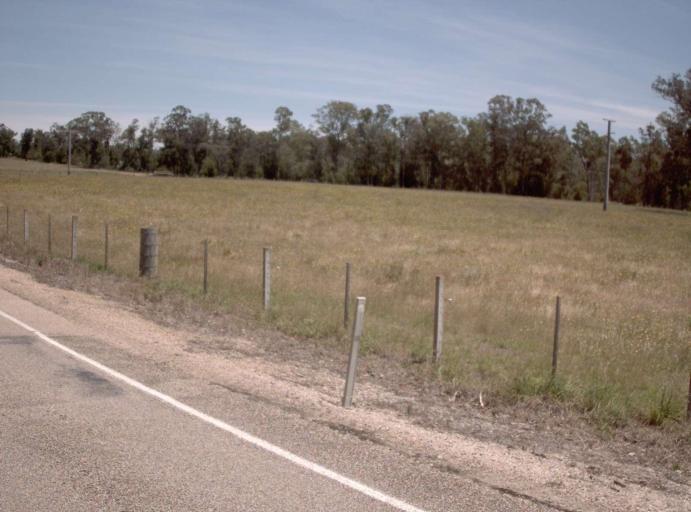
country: AU
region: Victoria
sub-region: East Gippsland
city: Lakes Entrance
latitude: -37.6793
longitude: 147.8488
